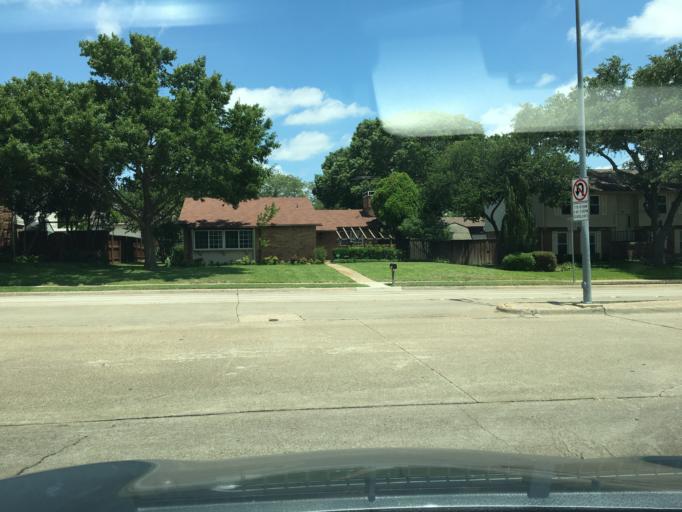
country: US
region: Texas
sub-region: Dallas County
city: Richardson
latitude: 32.9686
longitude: -96.6879
